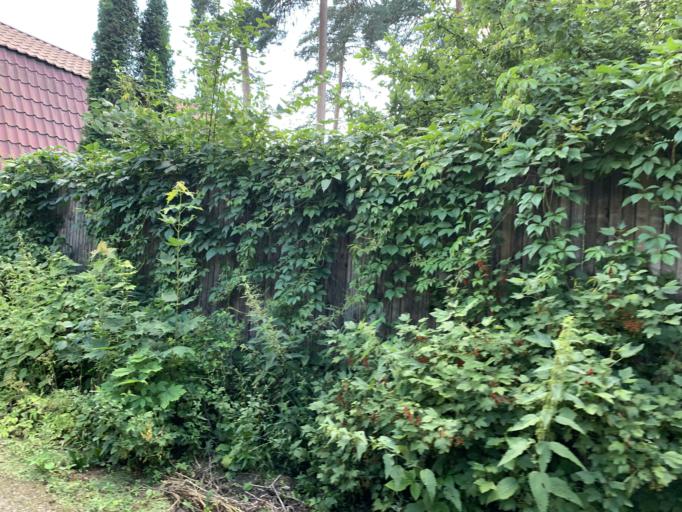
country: RU
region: Moskovskaya
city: Mamontovka
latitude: 55.9773
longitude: 37.8337
